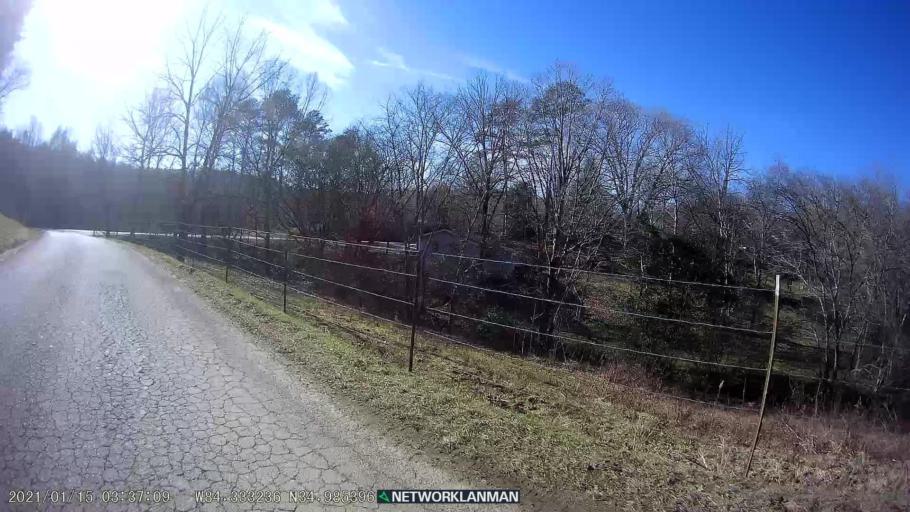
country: US
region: Georgia
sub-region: Fannin County
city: McCaysville
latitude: 34.9853
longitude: -84.3333
